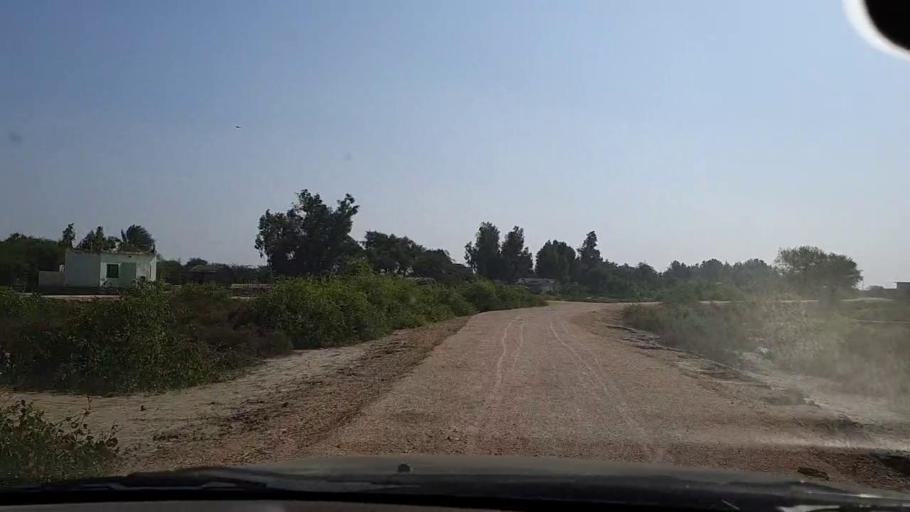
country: PK
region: Sindh
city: Chuhar Jamali
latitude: 24.3978
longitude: 67.8239
